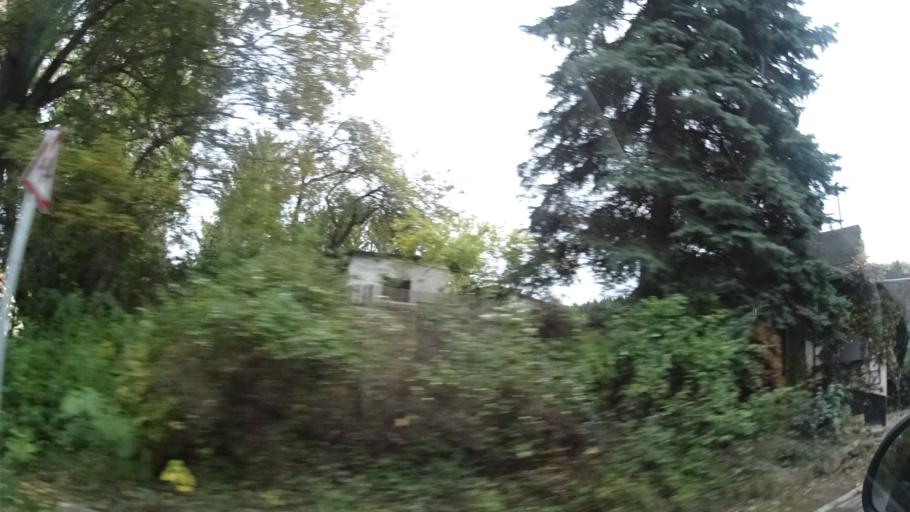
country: DE
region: Thuringia
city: Blankenhain
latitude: 50.8514
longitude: 11.3617
